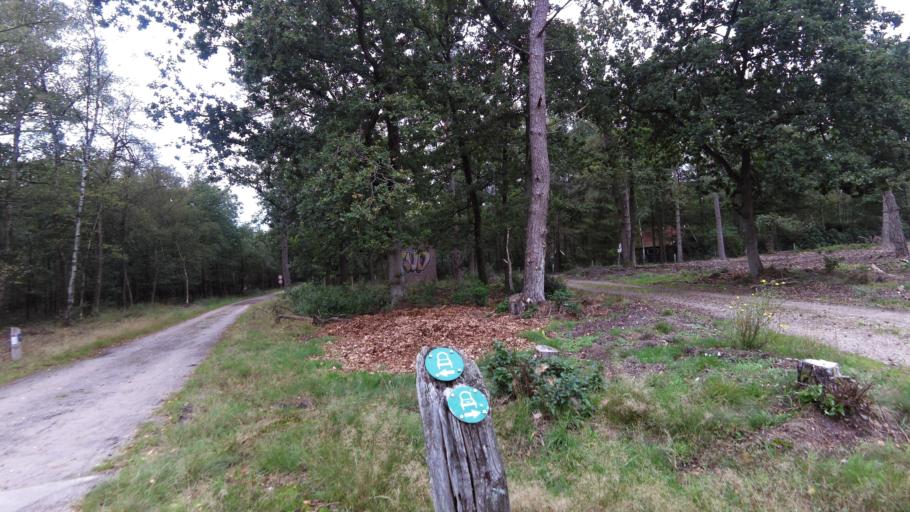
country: NL
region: Gelderland
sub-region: Gemeente Apeldoorn
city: Uddel
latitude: 52.1992
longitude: 5.8138
